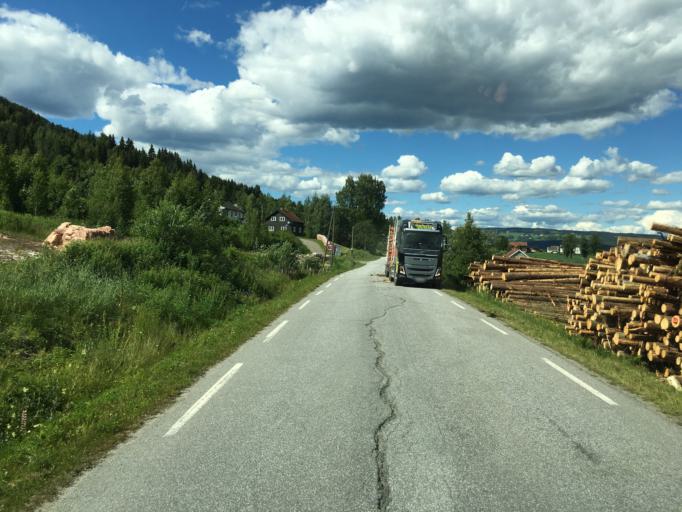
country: NO
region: Oppland
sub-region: Sondre Land
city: Hov
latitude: 60.6617
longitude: 10.3210
